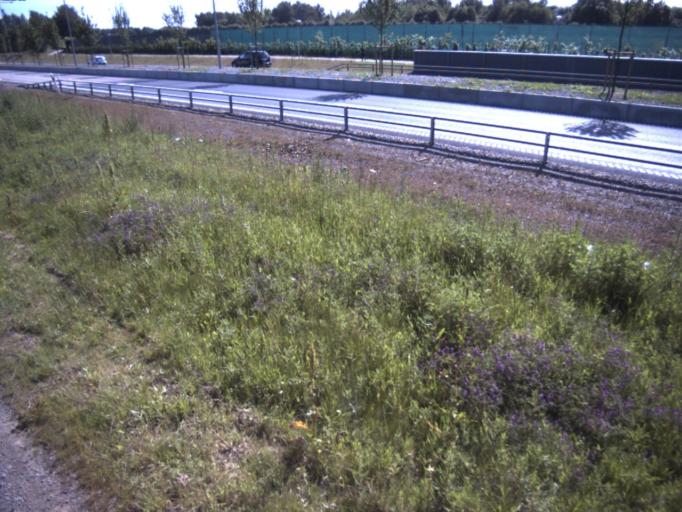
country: SE
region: Skane
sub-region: Helsingborg
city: Odakra
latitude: 56.0592
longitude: 12.7490
